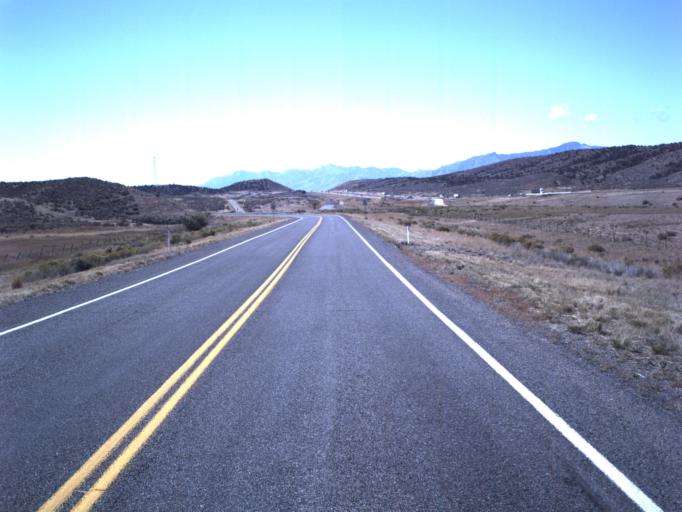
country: US
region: Utah
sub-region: Juab County
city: Nephi
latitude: 39.4857
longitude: -111.9723
